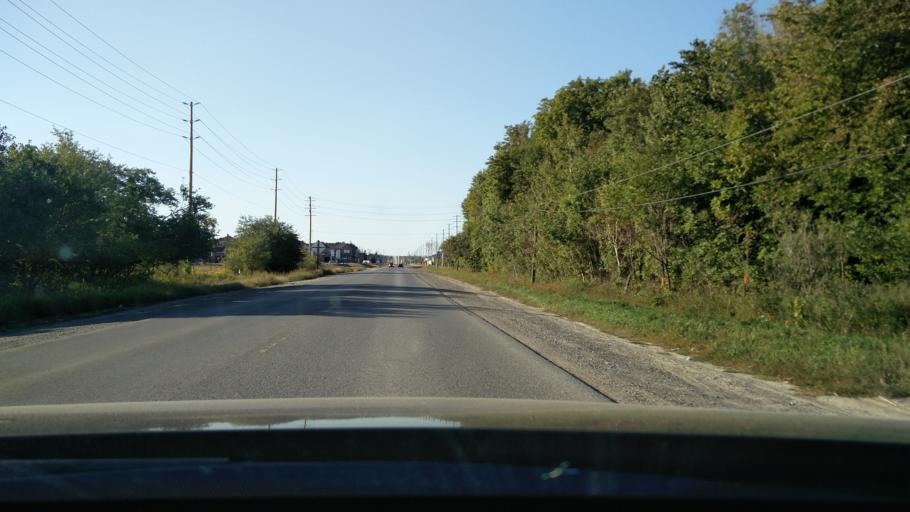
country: CA
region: Ontario
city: Bells Corners
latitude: 45.2377
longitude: -75.7268
